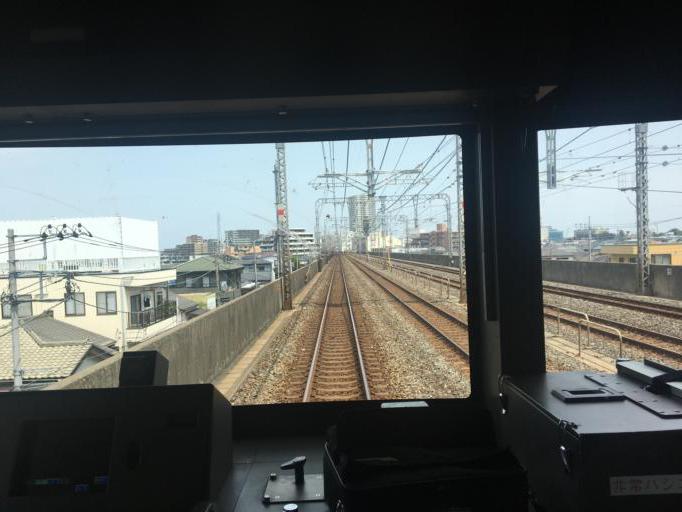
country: JP
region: Saitama
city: Koshigaya
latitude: 35.8805
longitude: 139.7887
